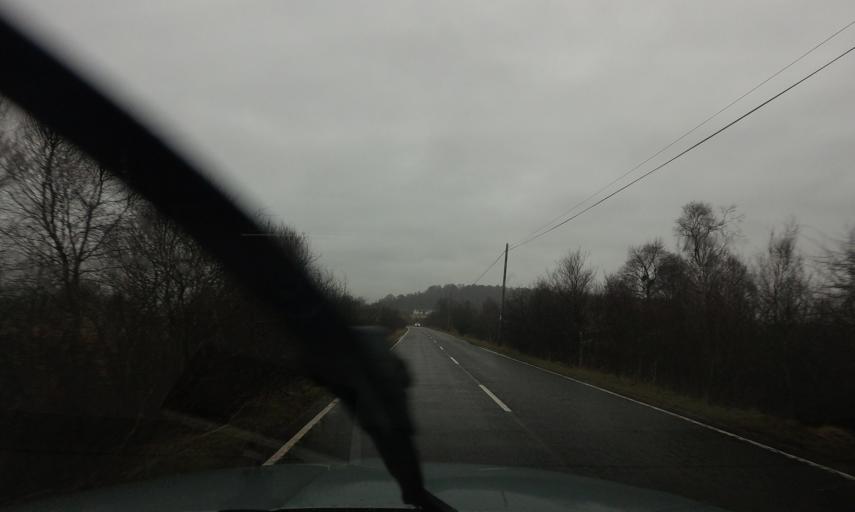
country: GB
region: Scotland
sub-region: Stirling
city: Balfron
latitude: 56.1339
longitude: -4.3581
